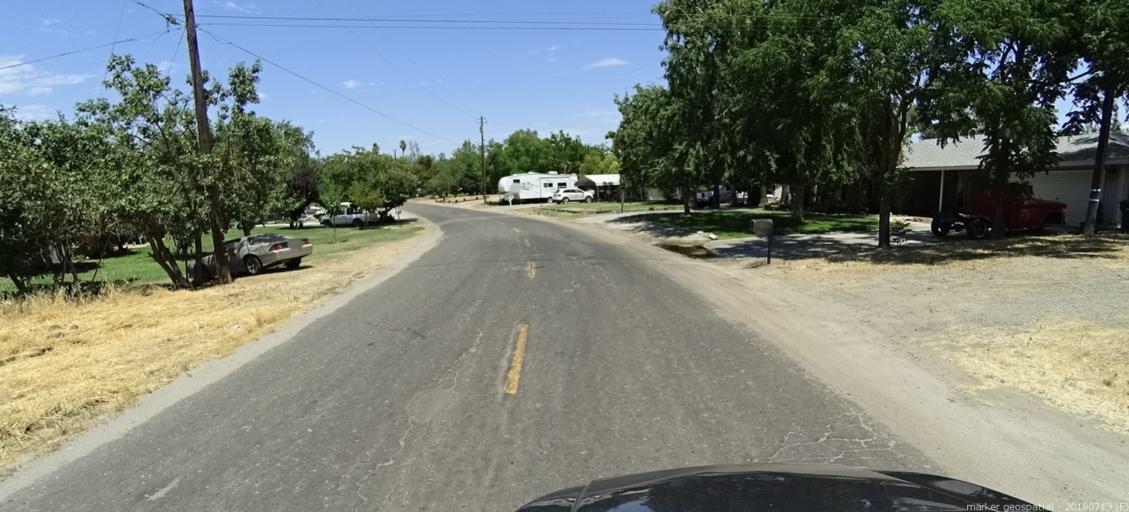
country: US
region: California
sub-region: Madera County
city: Madera Acres
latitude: 37.0147
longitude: -120.0765
